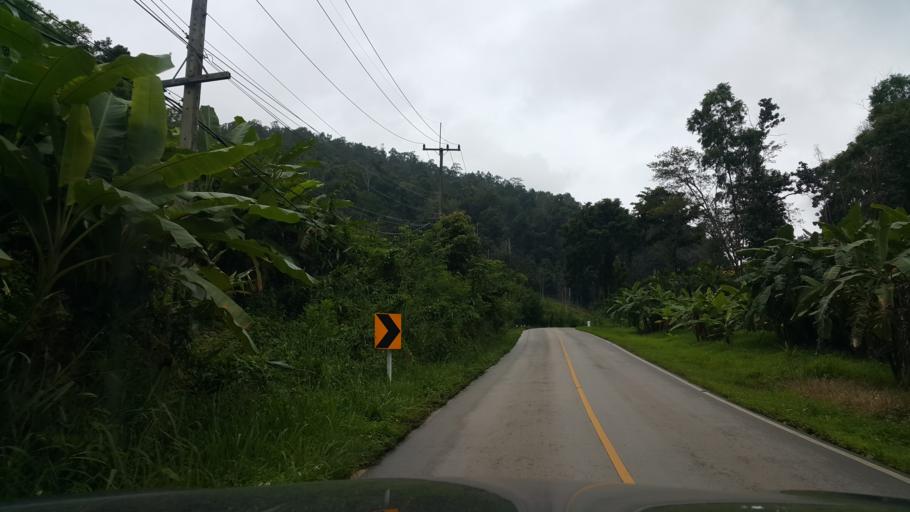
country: TH
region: Chiang Mai
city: Samoeng
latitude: 18.8659
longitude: 98.7175
